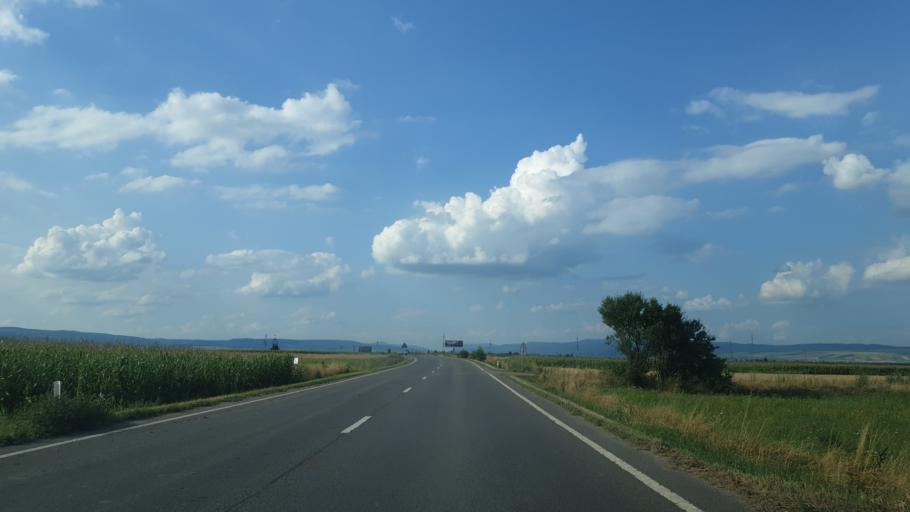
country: RO
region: Covasna
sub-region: Comuna Chichis
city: Chichis
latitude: 45.8178
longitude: 25.7990
